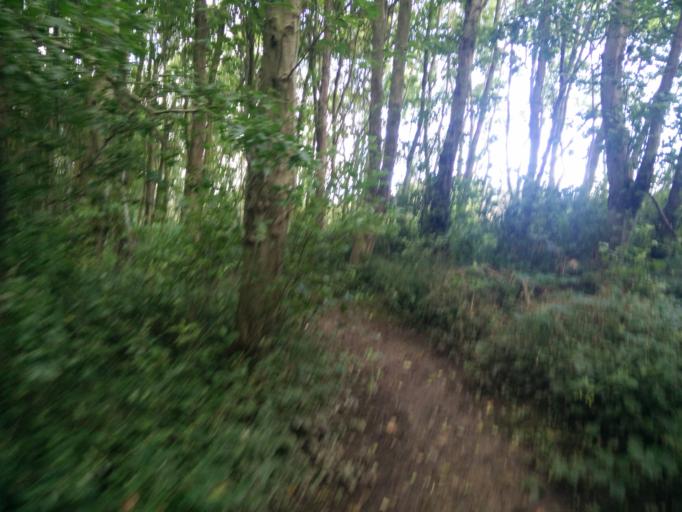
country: GB
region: England
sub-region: County Durham
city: Crook
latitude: 54.7231
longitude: -1.7657
